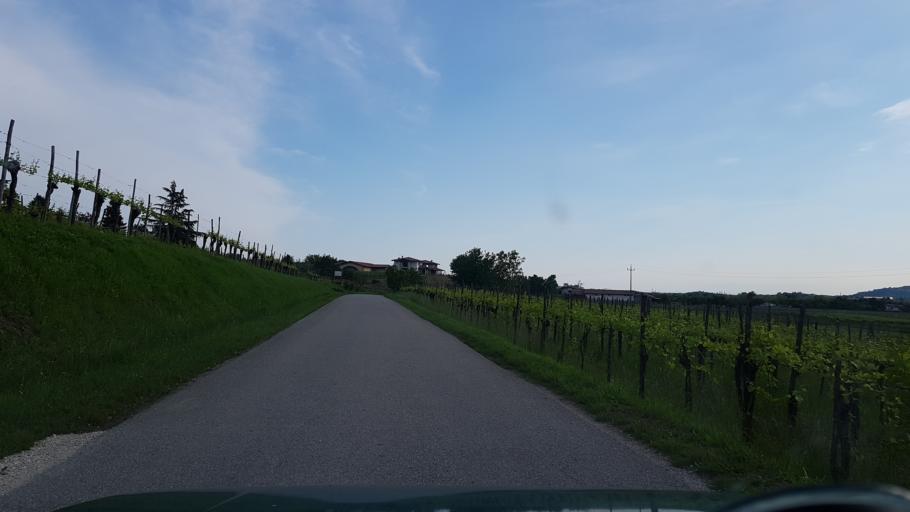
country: IT
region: Friuli Venezia Giulia
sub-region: Provincia di Gorizia
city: Cormons
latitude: 45.9546
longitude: 13.4846
